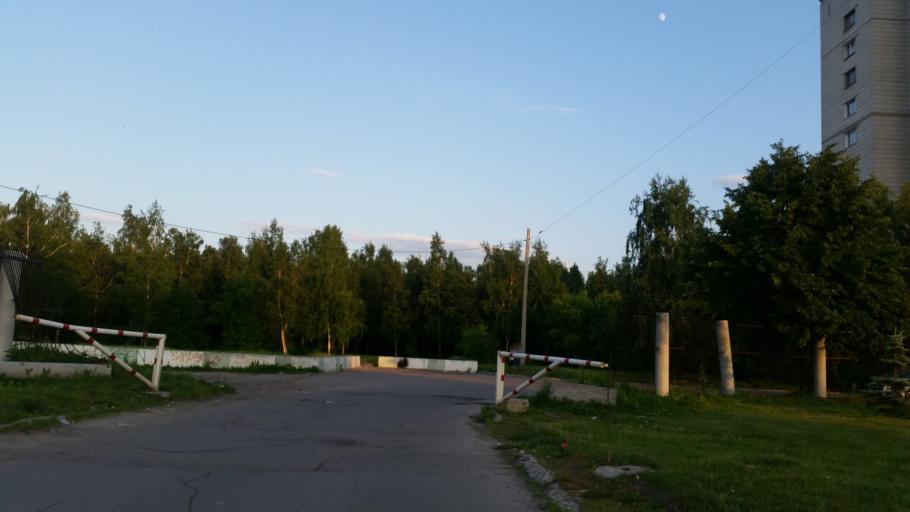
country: RU
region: Ulyanovsk
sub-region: Ulyanovskiy Rayon
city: Ulyanovsk
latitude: 54.3503
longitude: 48.3922
